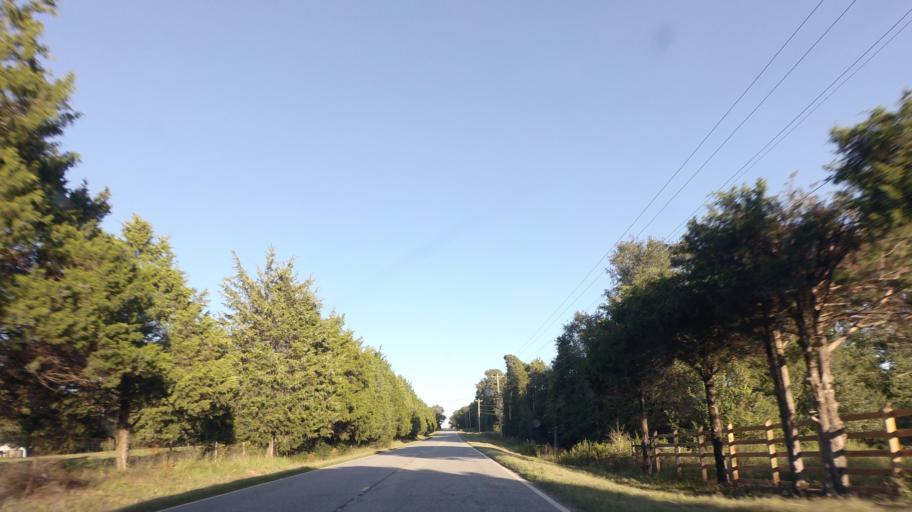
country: US
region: Georgia
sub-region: Henry County
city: Locust Grove
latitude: 33.2838
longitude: -84.1578
